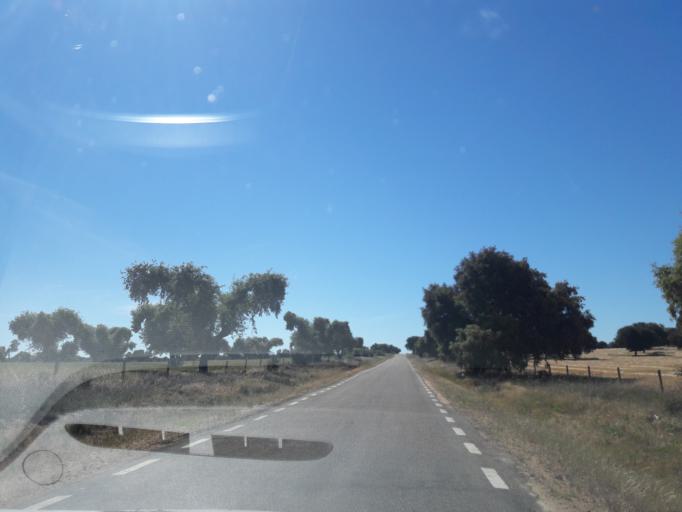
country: ES
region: Castille and Leon
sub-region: Provincia de Salamanca
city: Zarapicos
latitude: 41.0200
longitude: -5.8229
